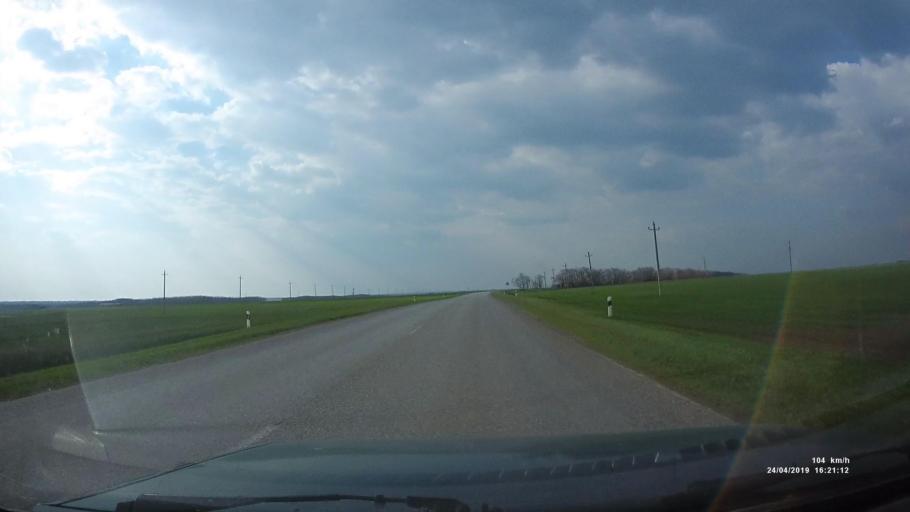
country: RU
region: Rostov
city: Orlovskiy
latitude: 46.8017
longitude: 42.0679
